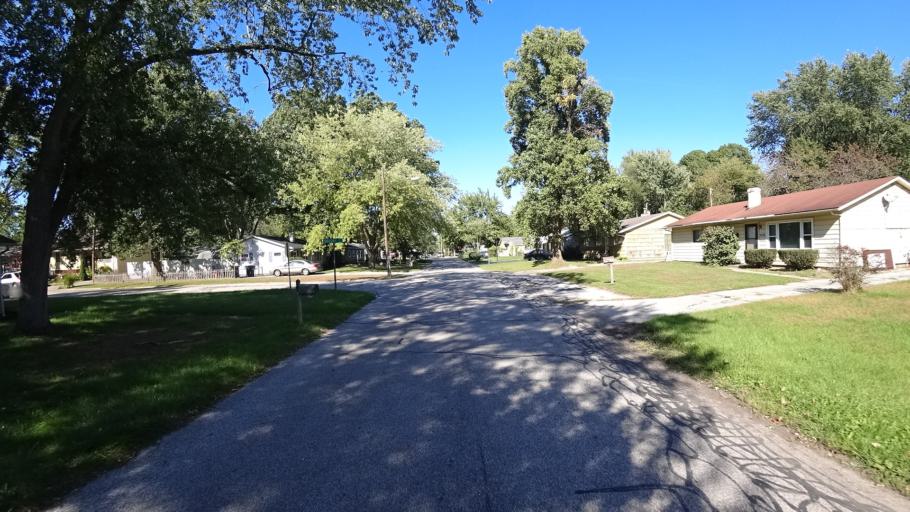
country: US
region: Indiana
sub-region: LaPorte County
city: Michigan City
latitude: 41.6910
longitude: -86.8990
